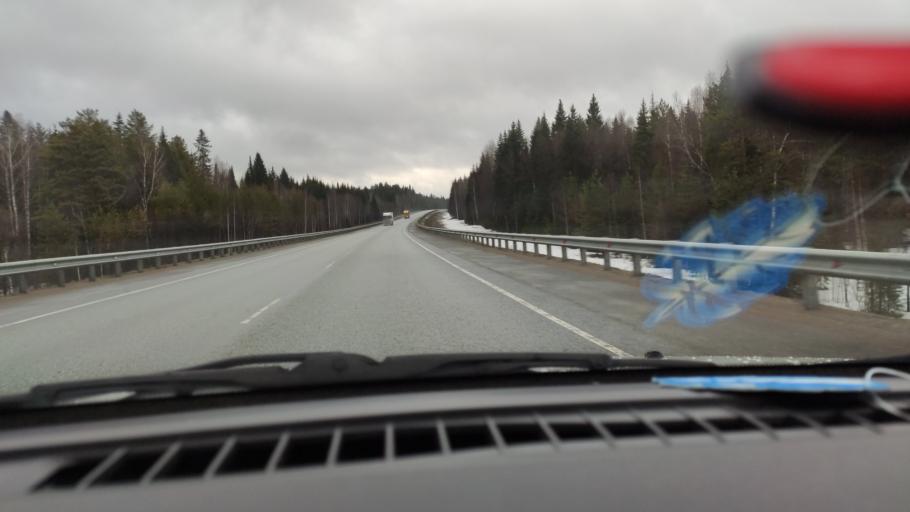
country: RU
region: Sverdlovsk
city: Achit
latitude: 56.8296
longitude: 57.7893
